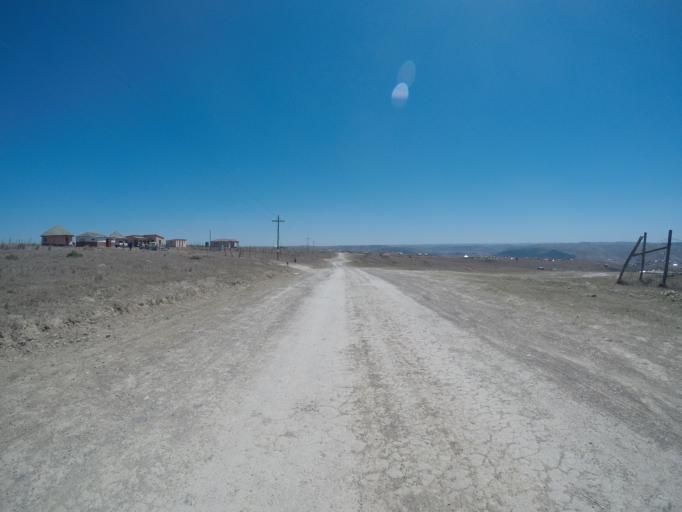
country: ZA
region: Eastern Cape
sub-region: OR Tambo District Municipality
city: Mthatha
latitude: -31.8927
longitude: 28.8859
